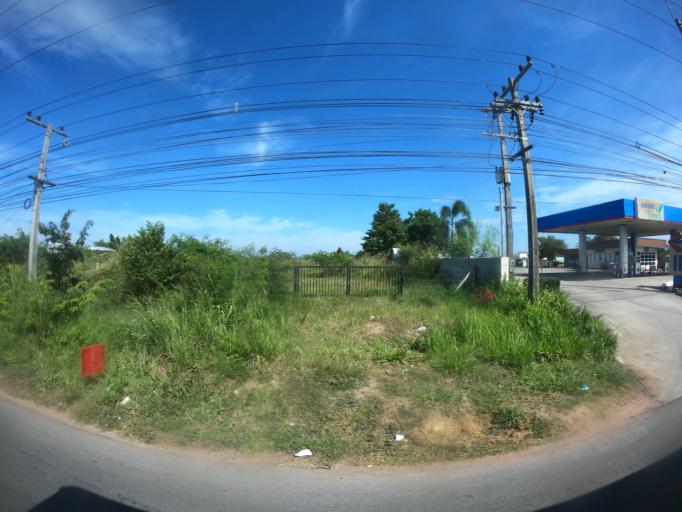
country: TH
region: Khon Kaen
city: Khon Kaen
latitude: 16.4378
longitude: 102.9284
